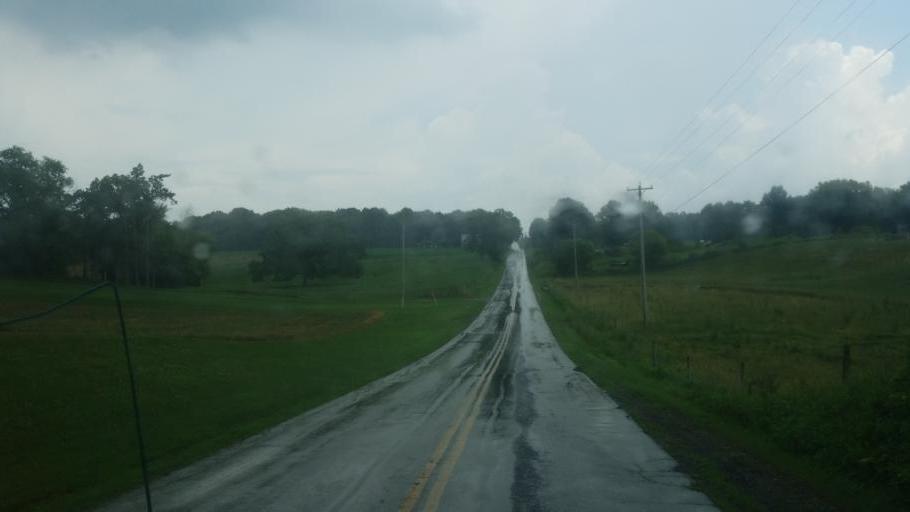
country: US
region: Ohio
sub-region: Wayne County
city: Smithville
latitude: 40.9018
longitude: -81.8164
